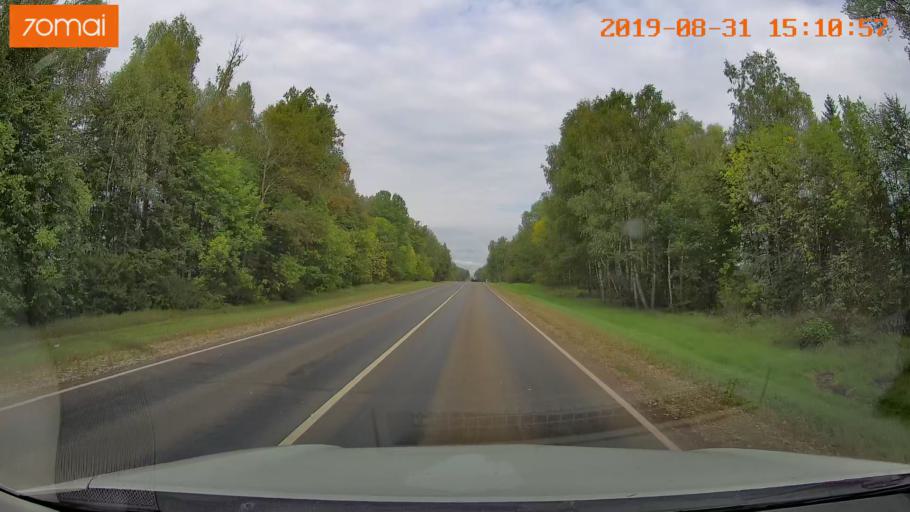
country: RU
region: Kaluga
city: Spas-Demensk
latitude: 54.4184
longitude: 34.2321
